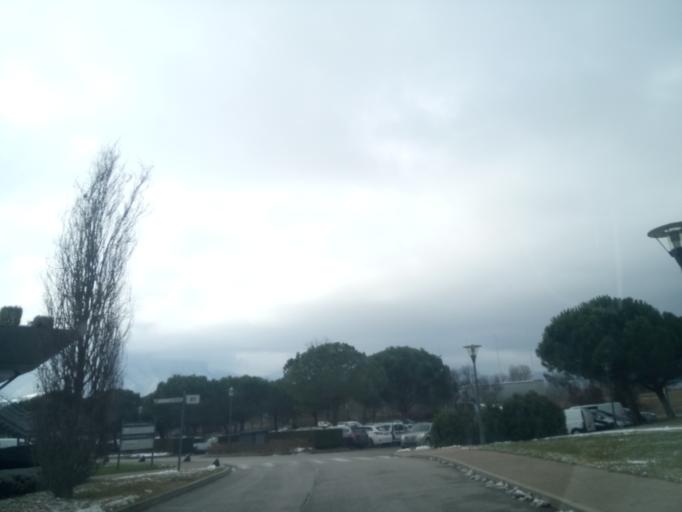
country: FR
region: Rhone-Alpes
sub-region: Departement de la Savoie
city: Montmelian
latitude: 45.4806
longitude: 6.0336
